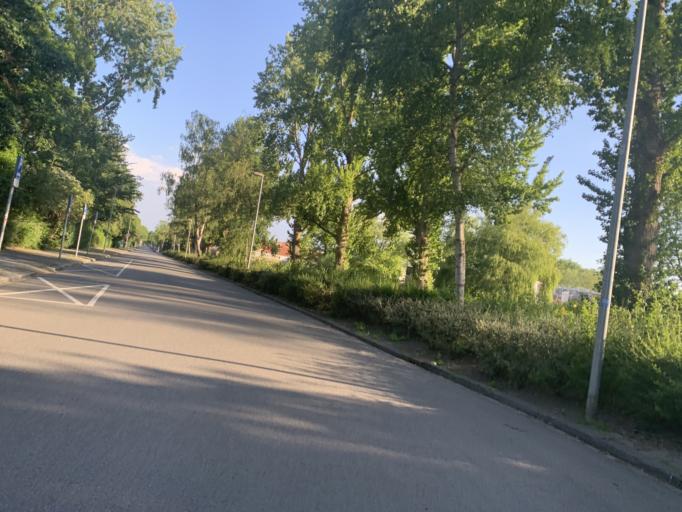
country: NL
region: Groningen
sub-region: Gemeente Groningen
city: Oosterpark
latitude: 53.2043
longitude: 6.5834
